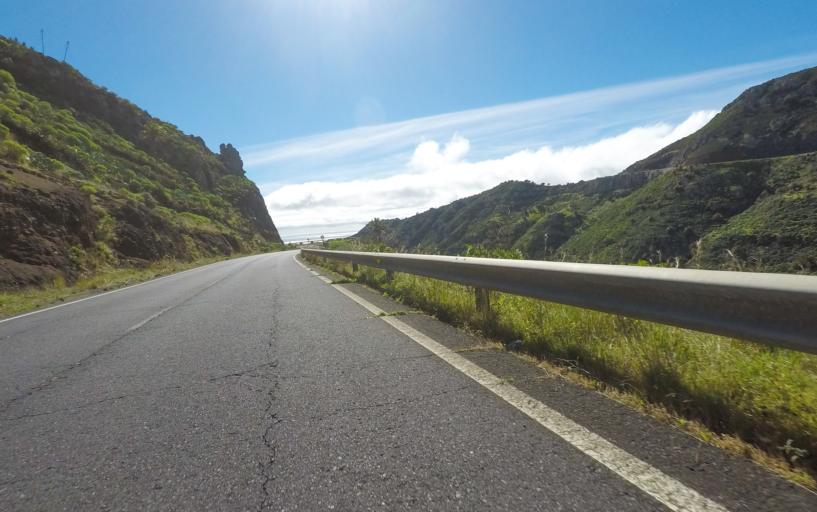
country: ES
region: Canary Islands
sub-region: Provincia de Santa Cruz de Tenerife
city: Alajero
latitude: 28.0955
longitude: -17.1997
